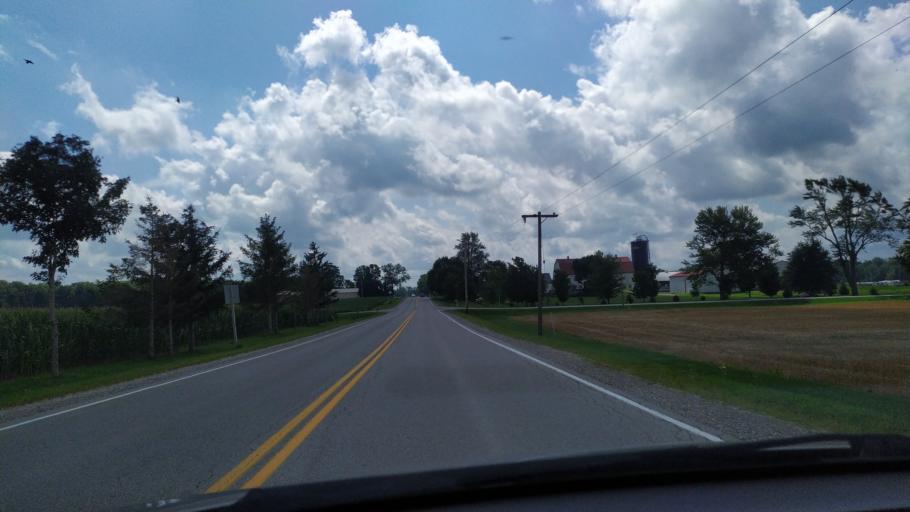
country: CA
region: Ontario
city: London
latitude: 43.0673
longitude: -81.3357
